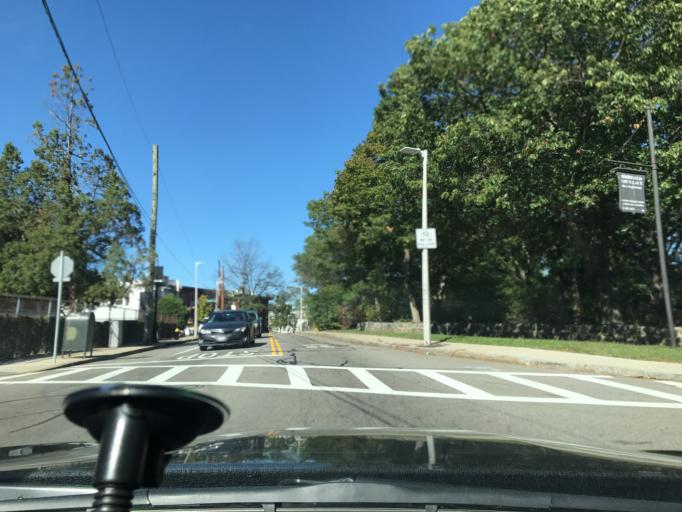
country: US
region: Massachusetts
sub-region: Suffolk County
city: Jamaica Plain
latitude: 42.3103
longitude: -71.0979
